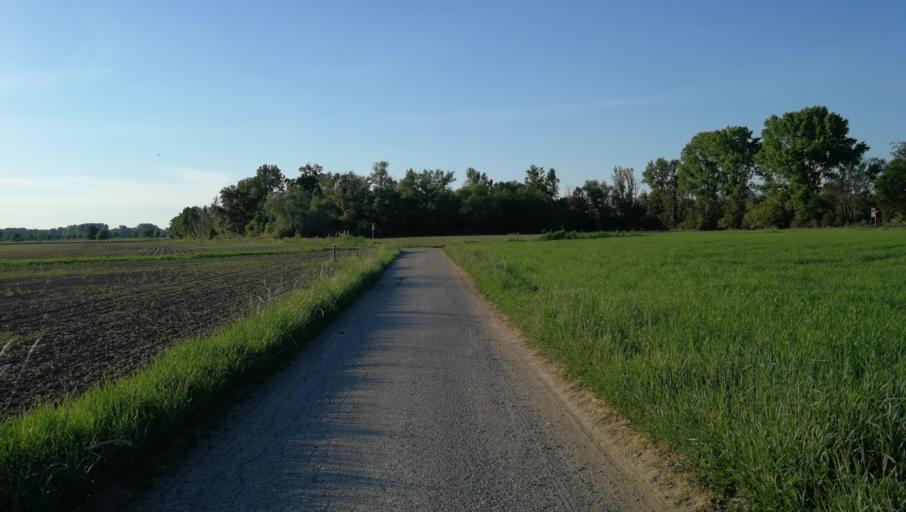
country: DE
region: Baden-Wuerttemberg
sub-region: Karlsruhe Region
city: Altlussheim
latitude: 49.3386
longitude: 8.5067
